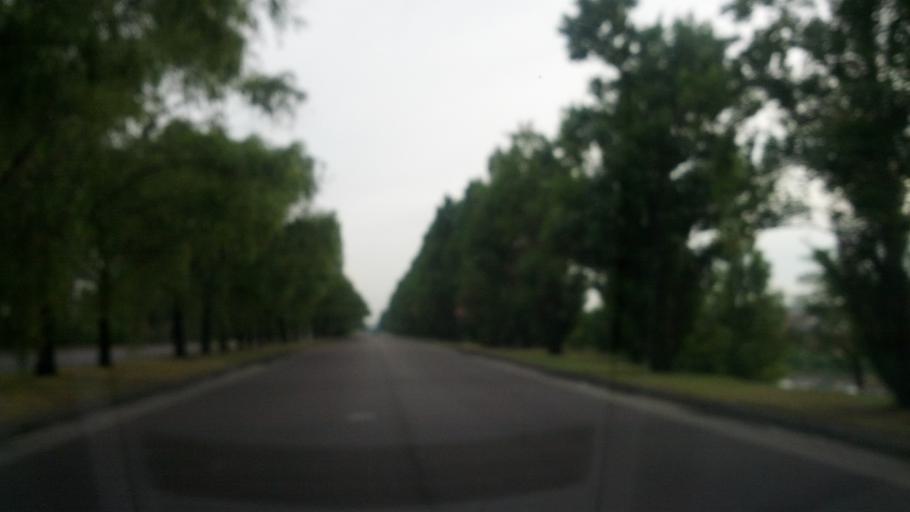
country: AR
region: Buenos Aires F.D.
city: Villa Lugano
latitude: -34.6878
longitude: -58.4468
